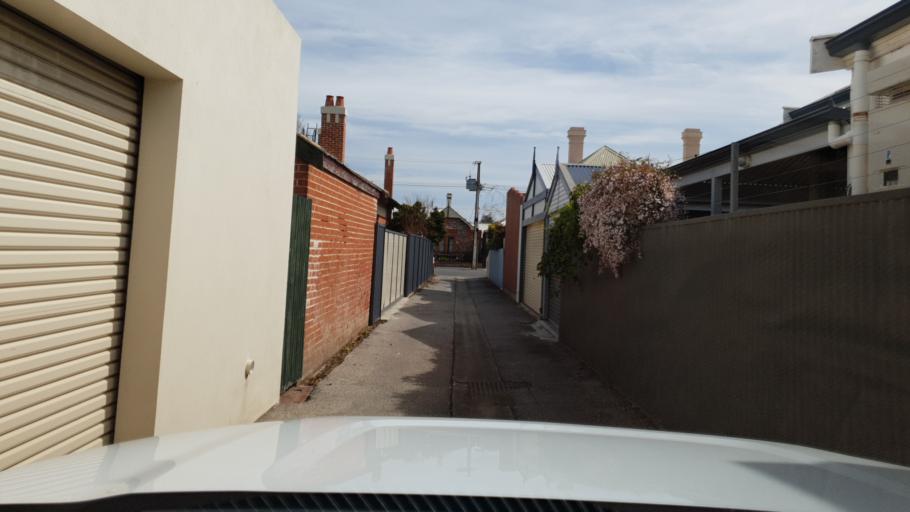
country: AU
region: South Australia
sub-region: Adelaide
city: Glenelg
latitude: -34.9870
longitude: 138.5160
